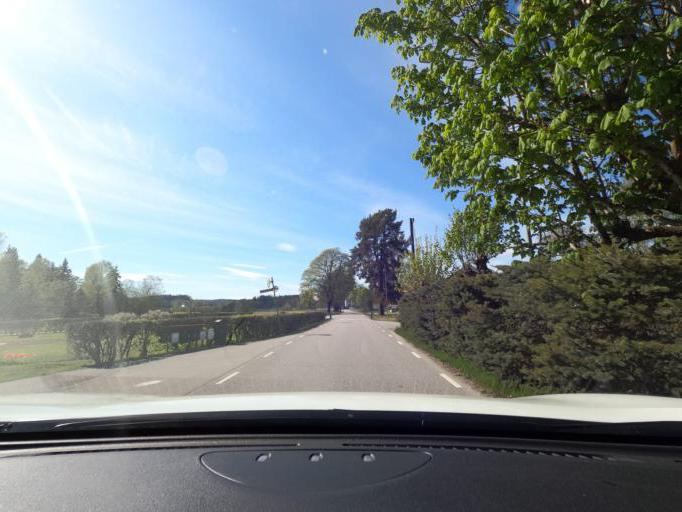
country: SE
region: Vaestra Goetaland
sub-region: Harryda Kommun
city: Ravlanda
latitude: 57.6481
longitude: 12.4926
